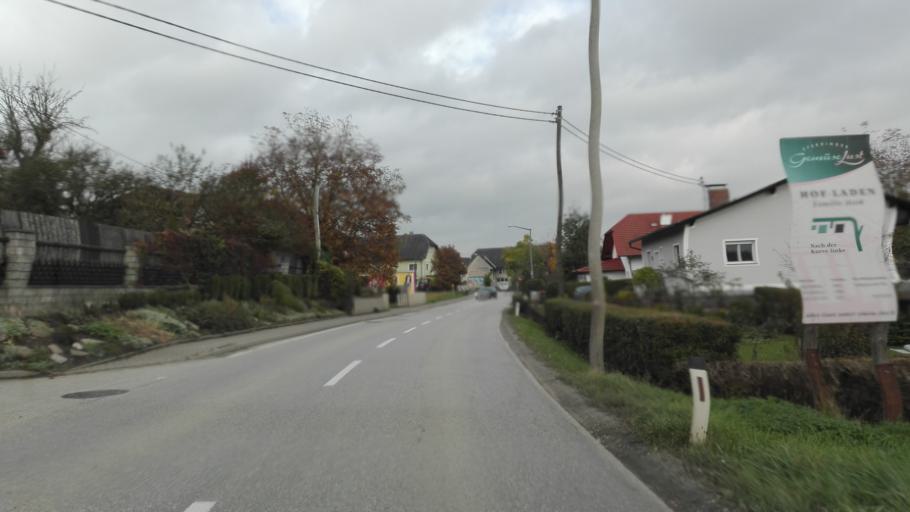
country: AT
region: Upper Austria
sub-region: Politischer Bezirk Urfahr-Umgebung
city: Feldkirchen an der Donau
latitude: 48.3494
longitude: 13.9954
